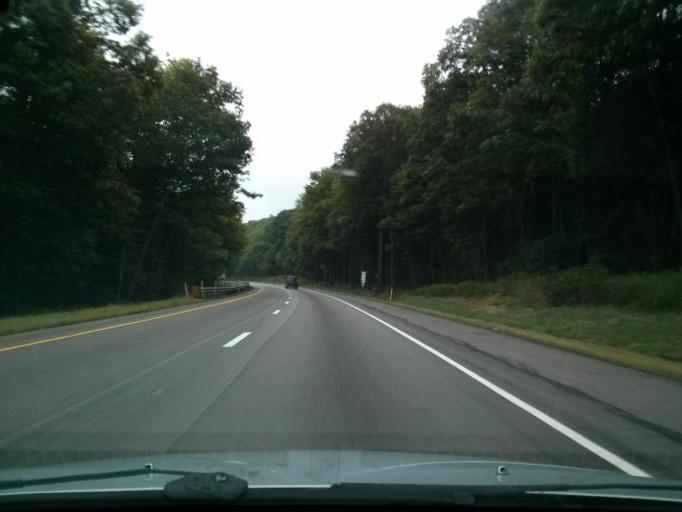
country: US
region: Pennsylvania
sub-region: Jefferson County
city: Brookville
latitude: 41.1474
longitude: -78.9960
